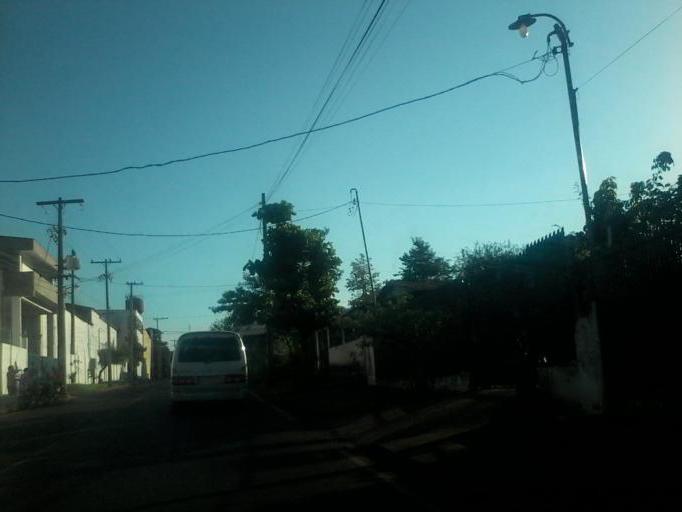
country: PY
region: Alto Parana
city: Ciudad del Este
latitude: -25.4990
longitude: -54.6328
